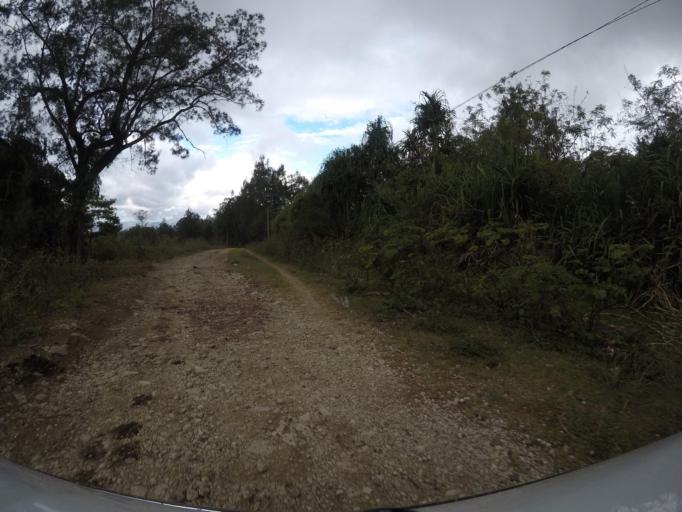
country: TL
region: Baucau
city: Venilale
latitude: -8.6718
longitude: 126.6292
